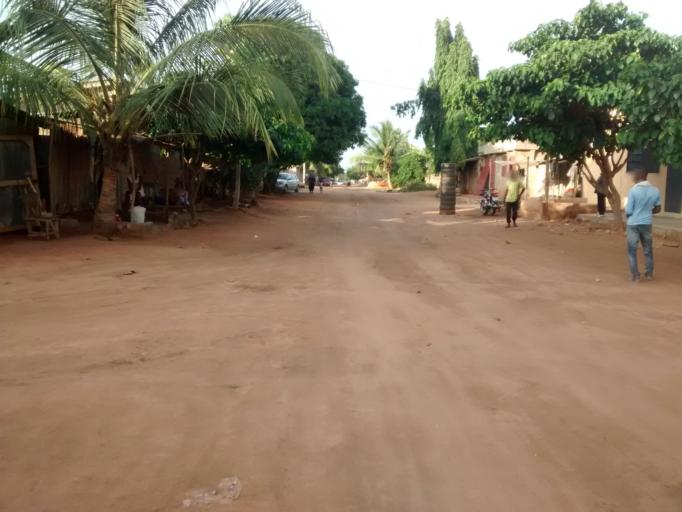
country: TG
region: Maritime
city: Lome
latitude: 6.1888
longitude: 1.1788
